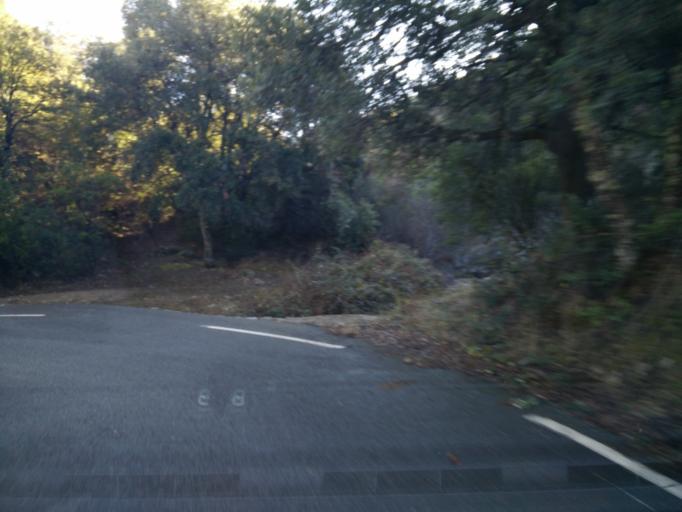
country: FR
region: Provence-Alpes-Cote d'Azur
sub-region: Departement du Var
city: Collobrieres
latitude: 43.2327
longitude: 6.3686
